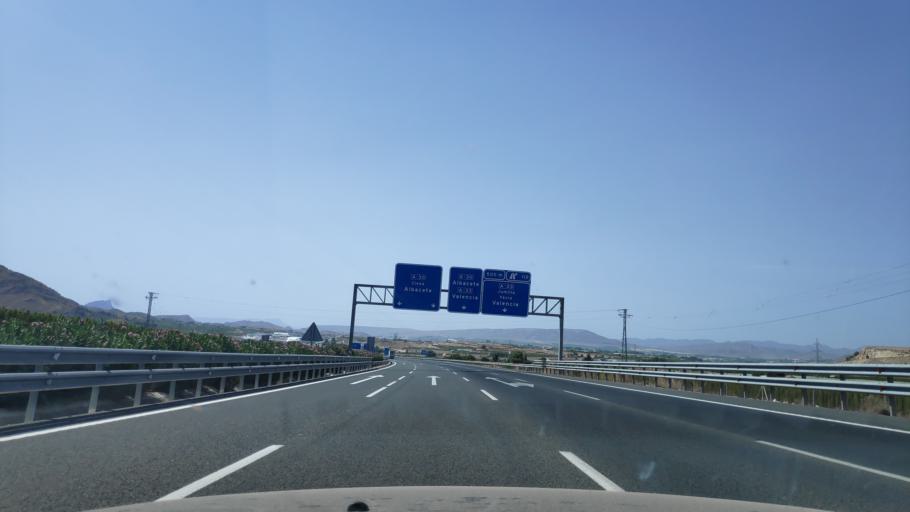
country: ES
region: Murcia
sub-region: Murcia
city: Ojos
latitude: 38.1814
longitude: -1.3172
